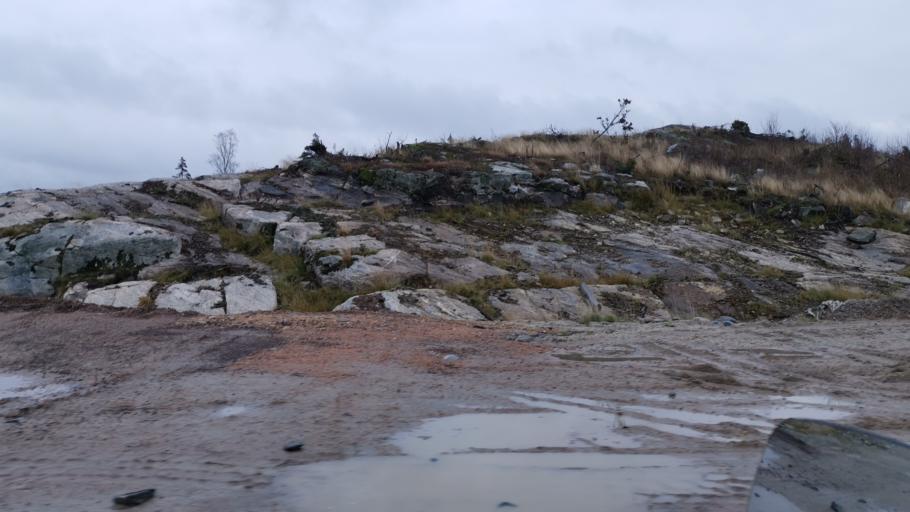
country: SE
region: Vaestra Goetaland
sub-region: Orust
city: Henan
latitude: 58.3500
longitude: 11.6988
